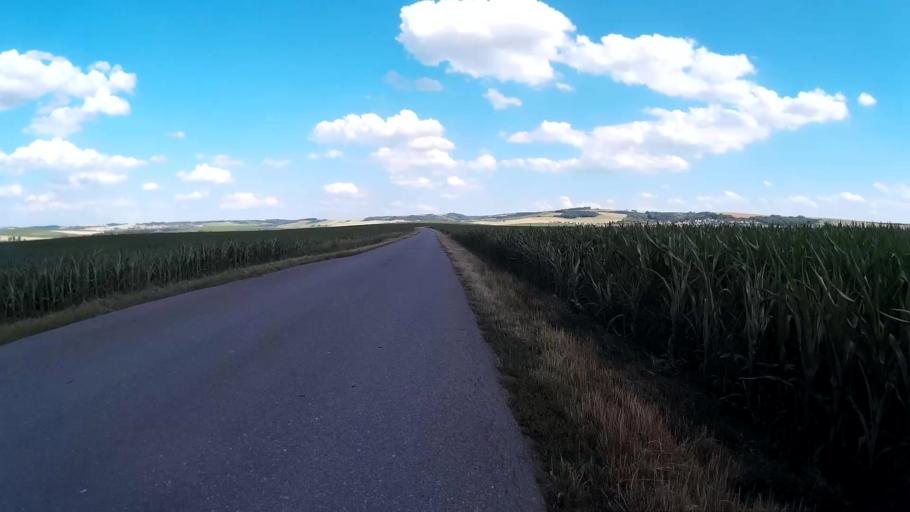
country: CZ
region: South Moravian
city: Krepice
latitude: 49.0176
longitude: 16.7059
